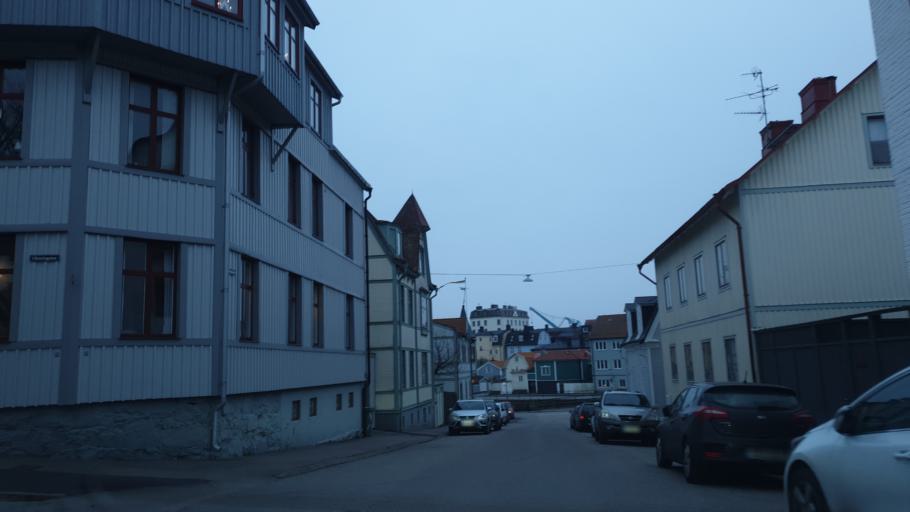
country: SE
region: Blekinge
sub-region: Karlskrona Kommun
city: Karlskrona
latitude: 56.1648
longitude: 15.5721
